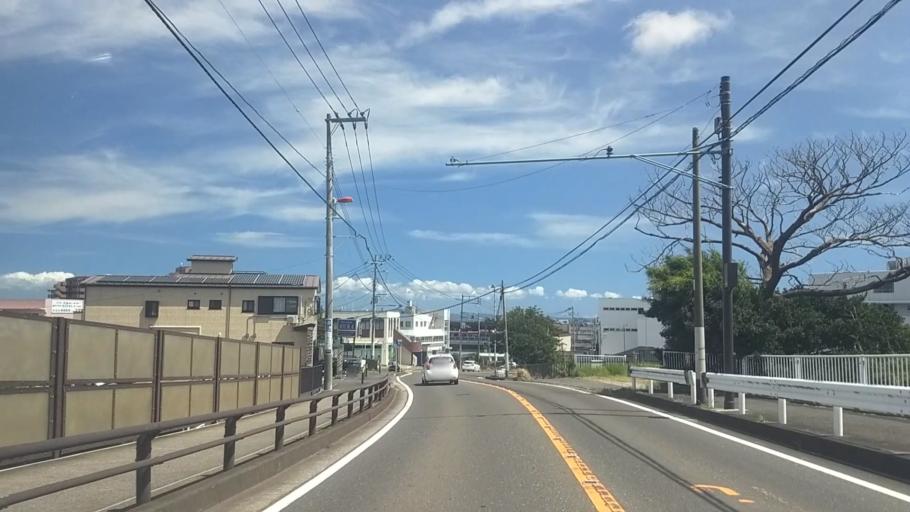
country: JP
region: Kanagawa
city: Miura
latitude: 35.1891
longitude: 139.6507
